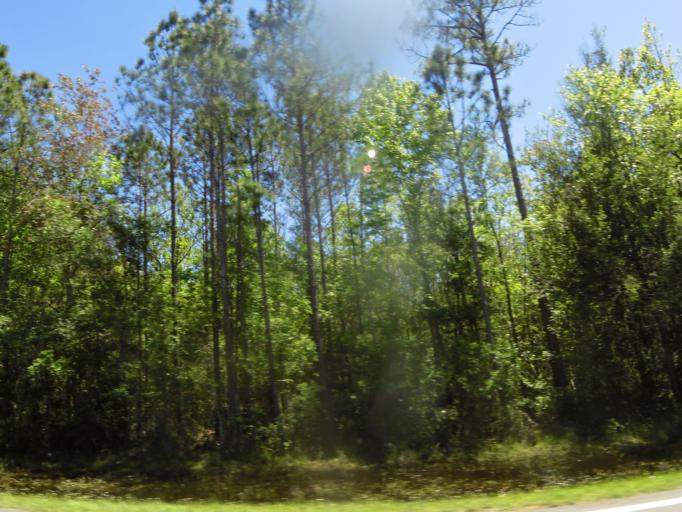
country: US
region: Florida
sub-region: Clay County
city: Green Cove Springs
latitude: 30.0208
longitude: -81.5996
